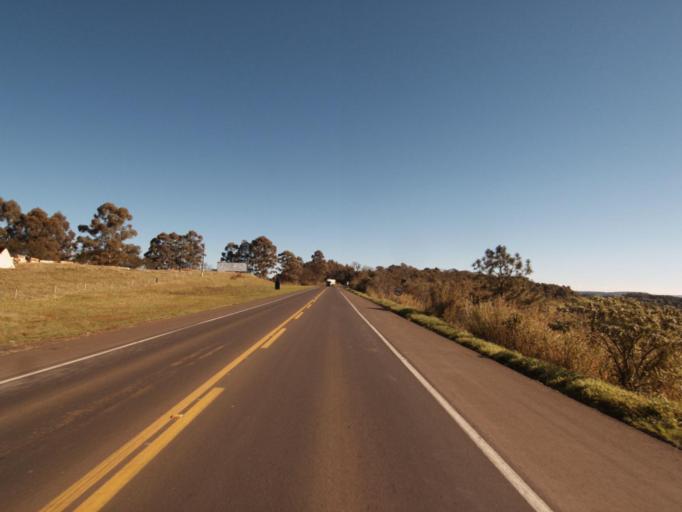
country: BR
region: Santa Catarina
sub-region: Chapeco
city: Chapeco
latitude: -26.9796
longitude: -52.5896
